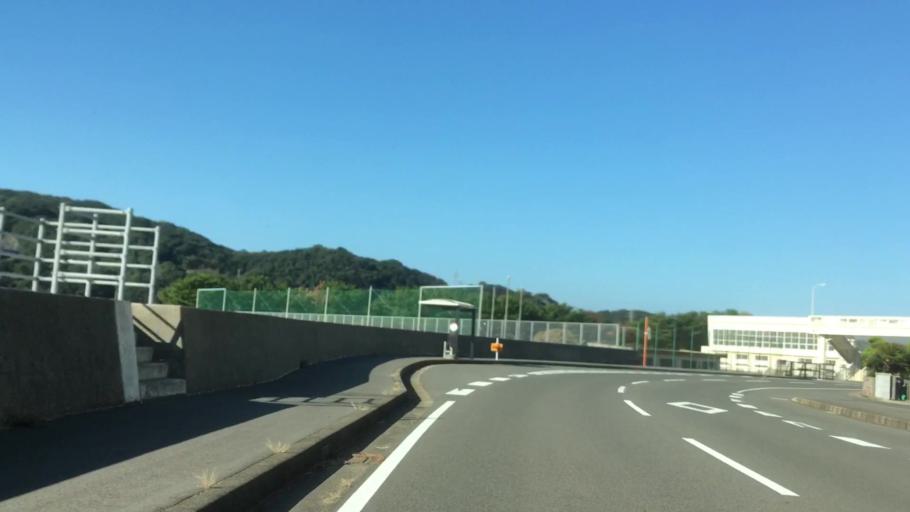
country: JP
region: Nagasaki
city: Sasebo
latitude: 33.0277
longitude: 129.5902
